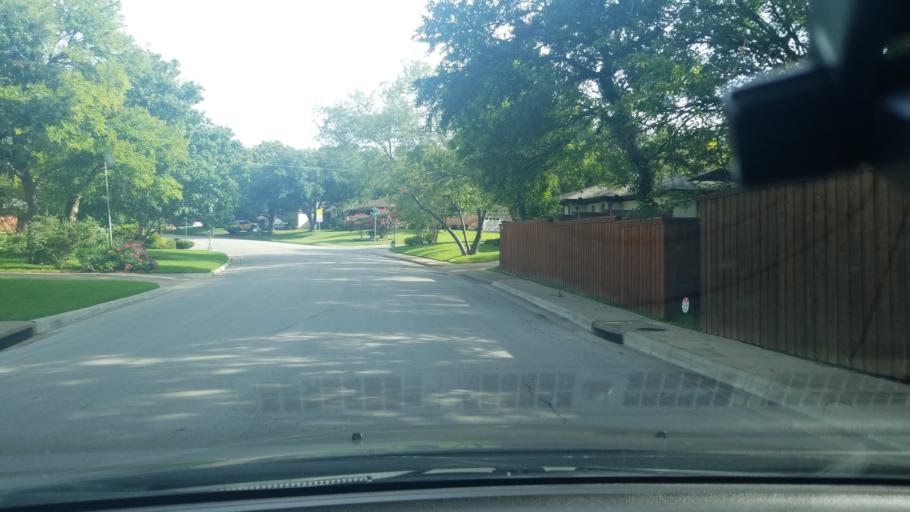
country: US
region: Texas
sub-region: Dallas County
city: Highland Park
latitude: 32.8019
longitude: -96.7084
